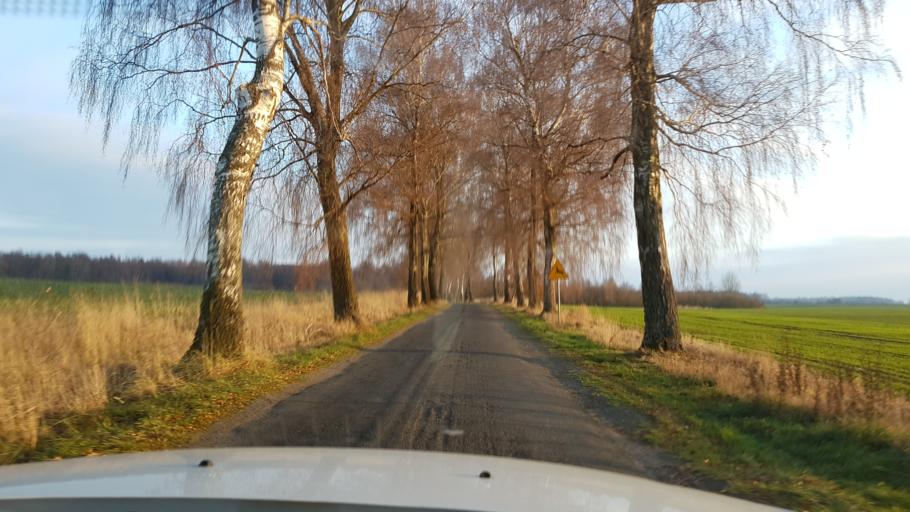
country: PL
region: West Pomeranian Voivodeship
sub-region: Koszalin
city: Koszalin
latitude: 54.1108
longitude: 16.1192
